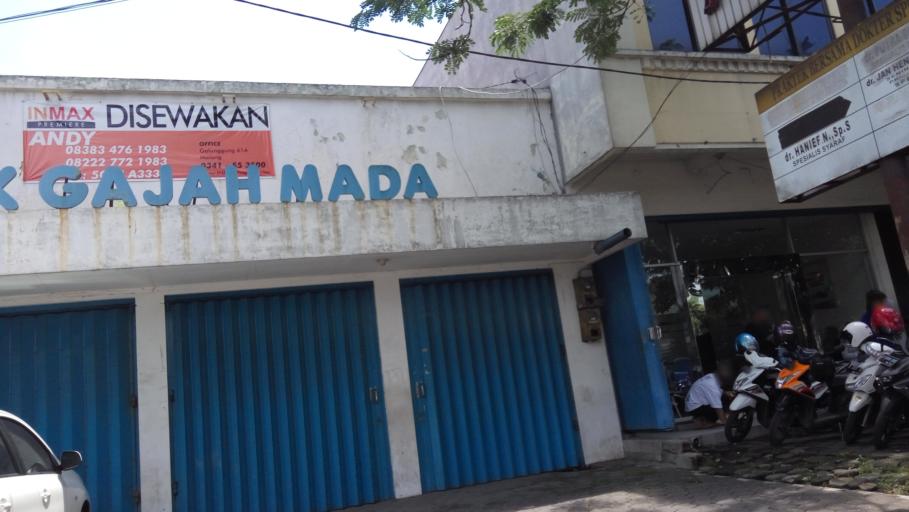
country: ID
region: East Java
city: Malang
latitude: -7.9611
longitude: 112.6367
